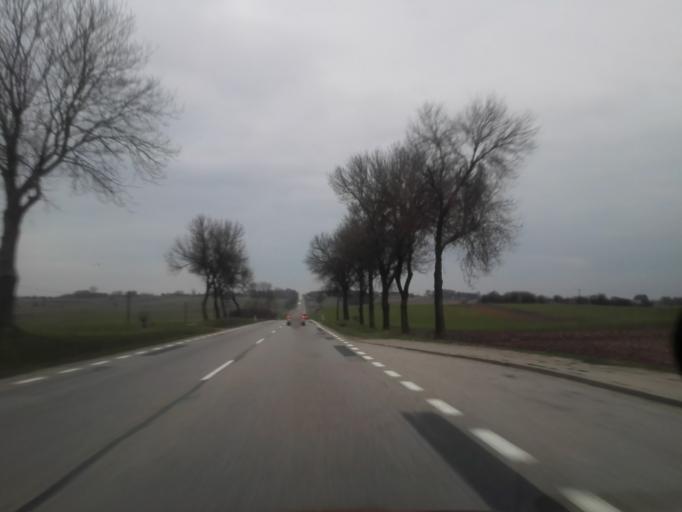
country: PL
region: Podlasie
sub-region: Powiat lomzynski
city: Piatnica
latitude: 53.2415
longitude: 22.1166
